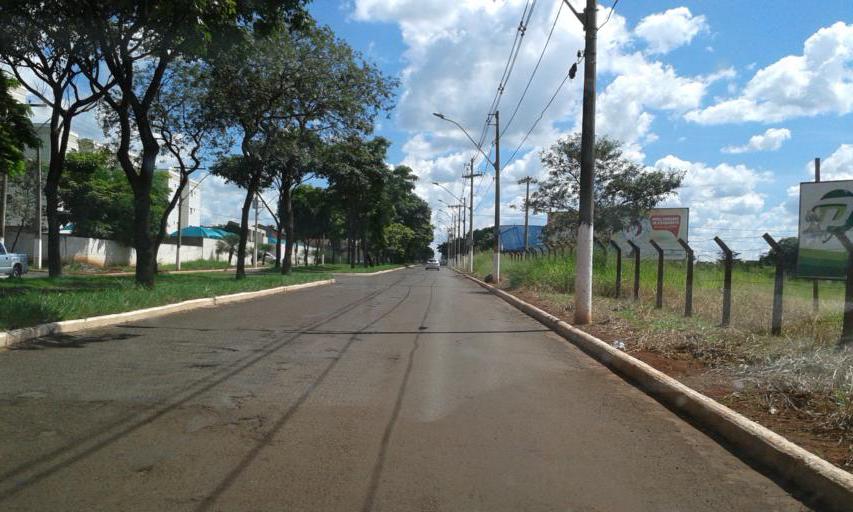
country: BR
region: Minas Gerais
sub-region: Ituiutaba
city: Ituiutaba
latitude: -18.9692
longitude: -49.4758
